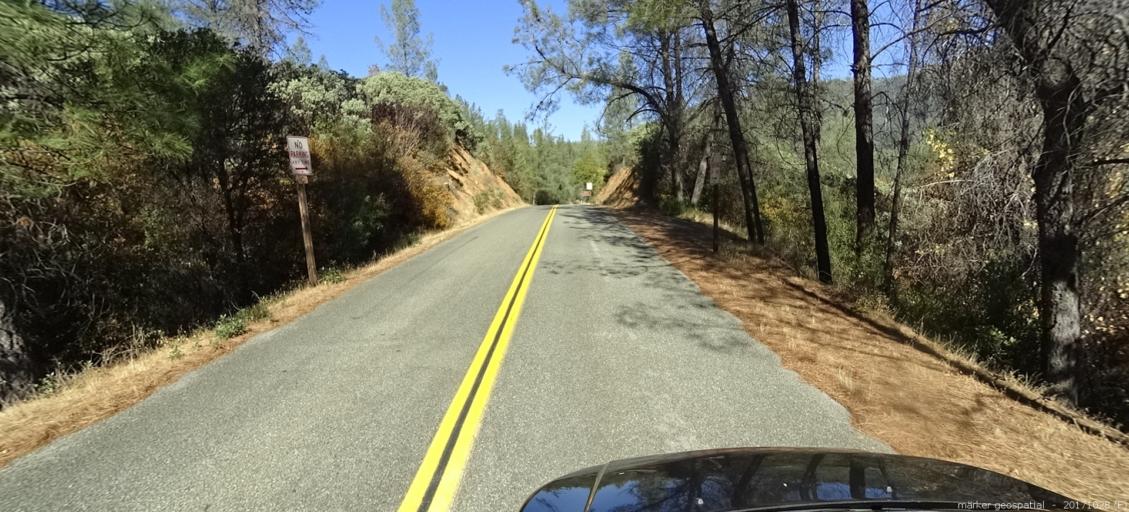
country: US
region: California
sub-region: Shasta County
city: Shasta
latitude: 40.6459
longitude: -122.5576
